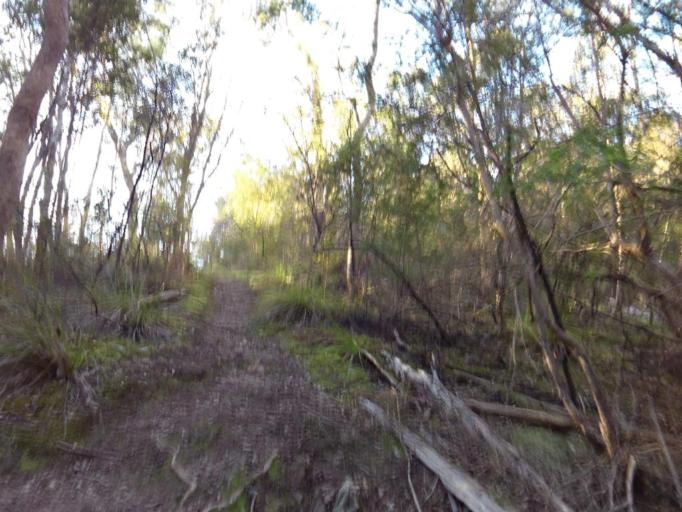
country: AU
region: Victoria
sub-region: Nillumbik
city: North Warrandyte
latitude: -37.7243
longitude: 145.2368
